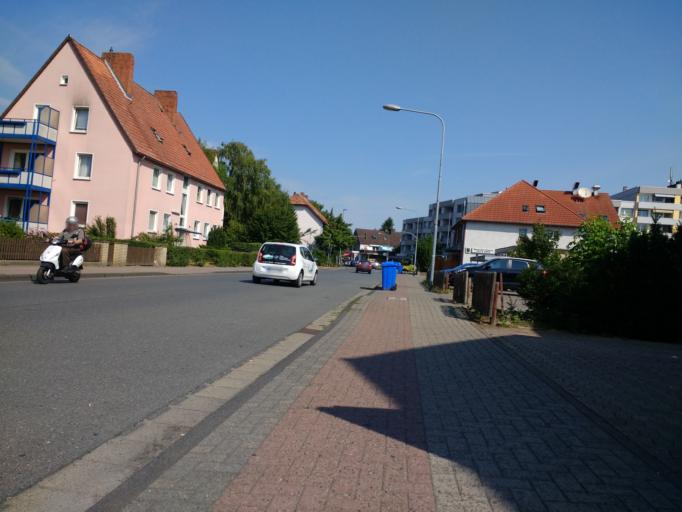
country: DE
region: Lower Saxony
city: Gifhorn
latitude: 52.4728
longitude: 10.5462
